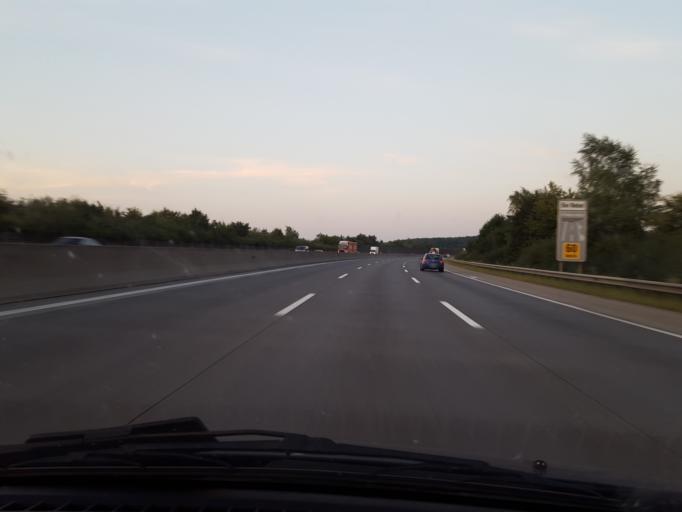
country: AT
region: Upper Austria
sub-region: Politischer Bezirk Linz-Land
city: Ansfelden
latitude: 48.2325
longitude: 14.3229
